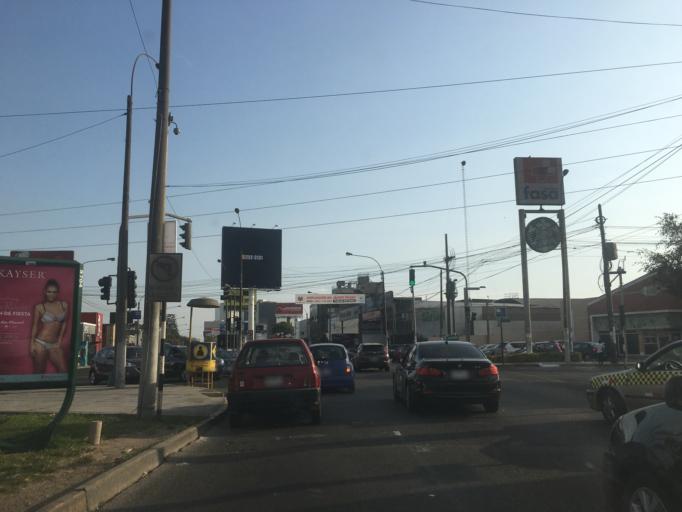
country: PE
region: Lima
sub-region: Lima
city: La Molina
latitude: -12.0752
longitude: -76.9635
